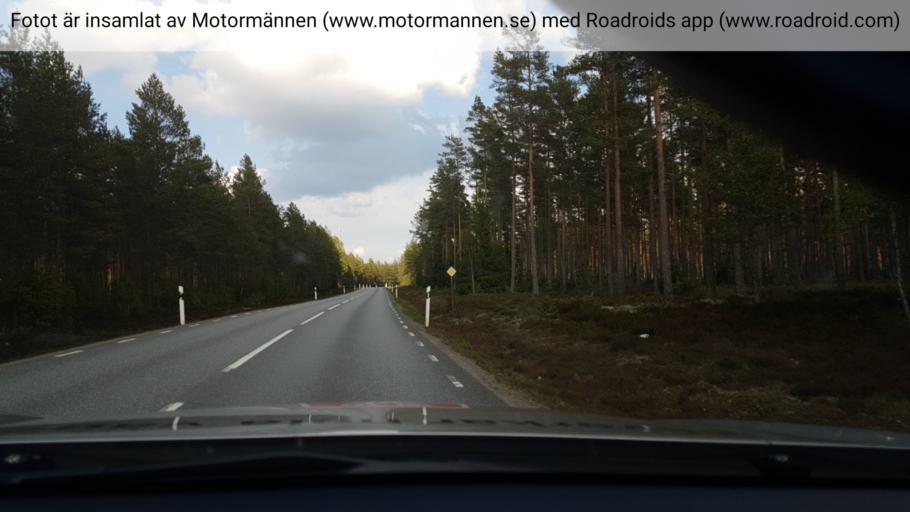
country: SE
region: Joenkoeping
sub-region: Vaggeryds Kommun
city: Skillingaryd
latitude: 57.3827
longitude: 13.9780
